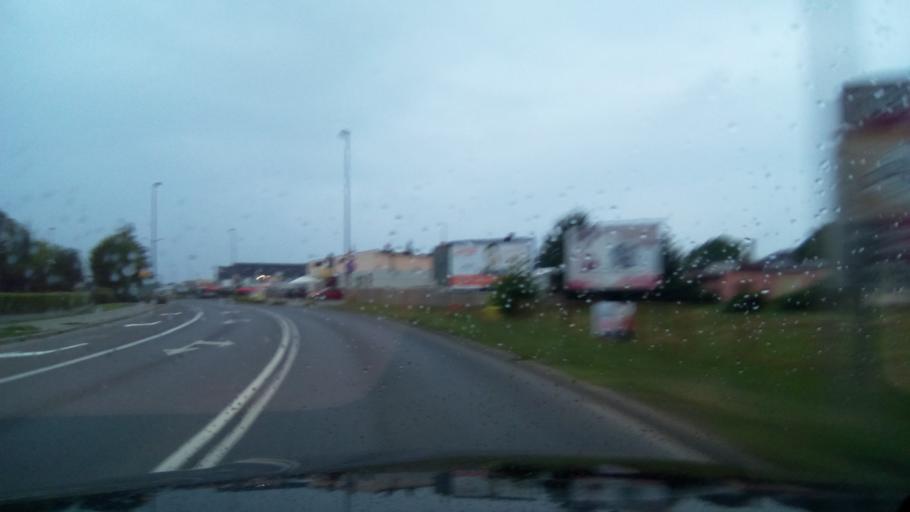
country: PL
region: Greater Poland Voivodeship
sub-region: Powiat poznanski
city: Swarzedz
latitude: 52.4158
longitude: 17.0859
